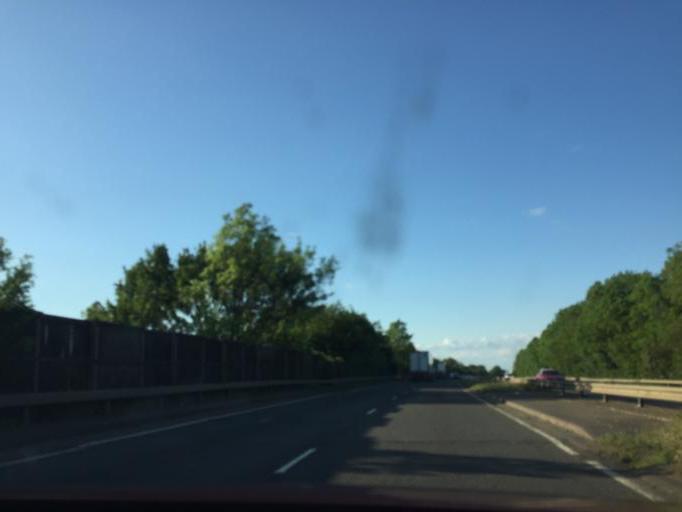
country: GB
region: England
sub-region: Warwickshire
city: Exhall
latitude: 52.4789
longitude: -1.4892
